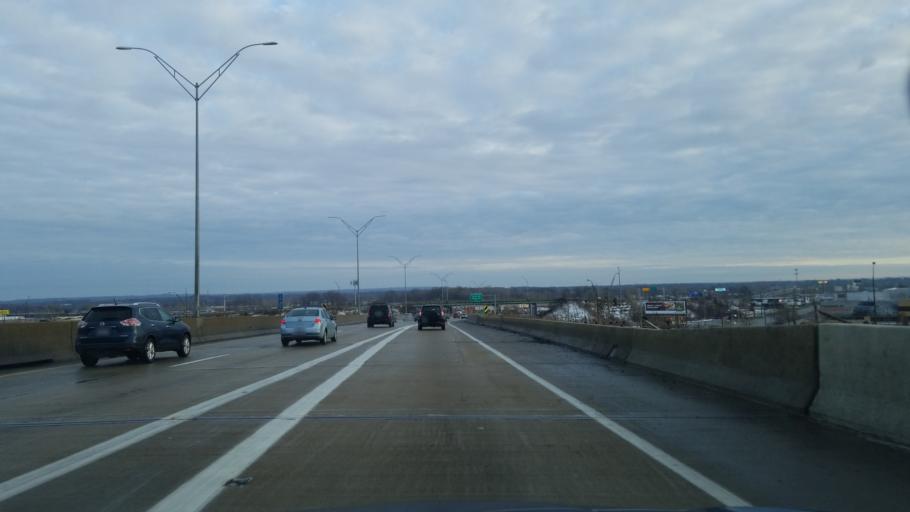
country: US
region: Ohio
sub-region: Cuyahoga County
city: Brook Park
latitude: 41.4216
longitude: -81.8198
